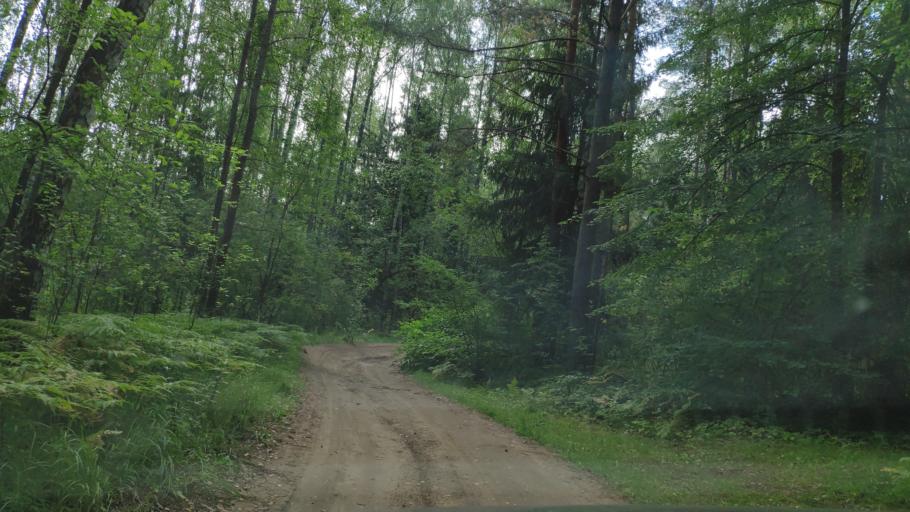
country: BY
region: Minsk
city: Khatsyezhyna
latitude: 53.9589
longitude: 27.3084
